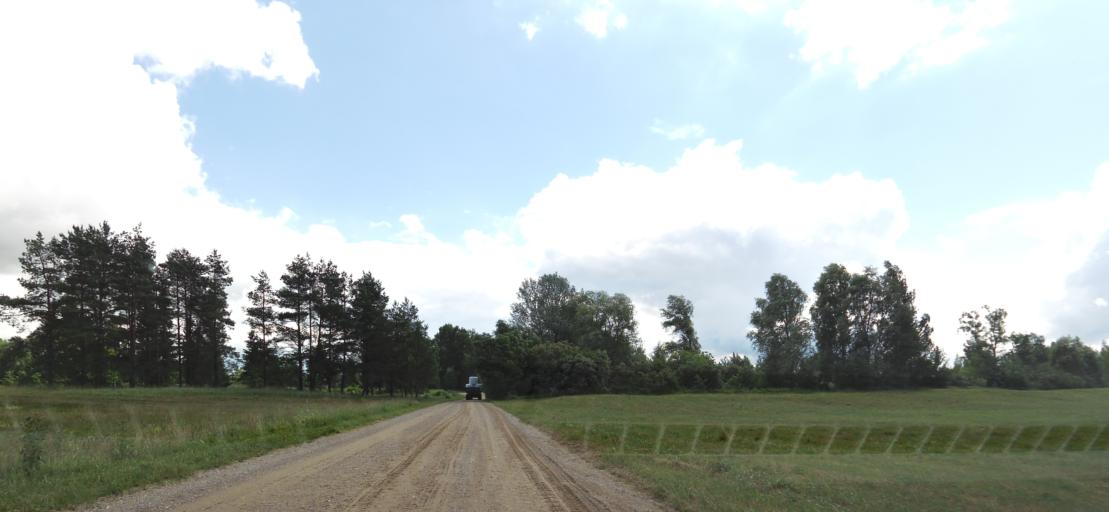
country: LT
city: Vabalninkas
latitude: 55.8812
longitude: 24.7774
